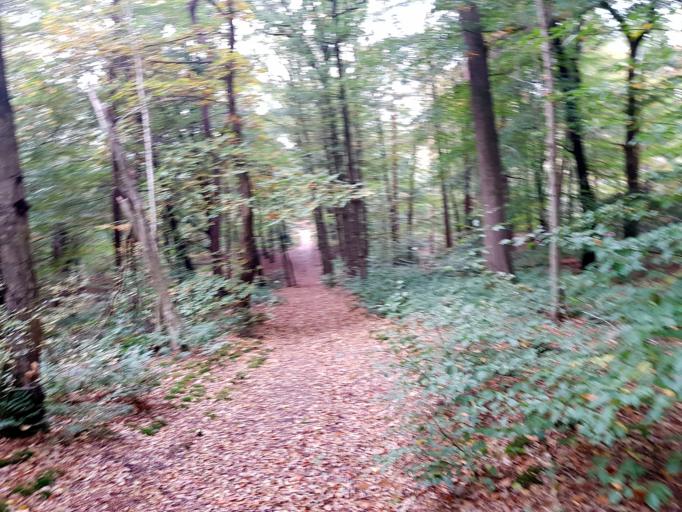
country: NL
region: Utrecht
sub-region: Gemeente Utrechtse Heuvelrug
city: Leersum
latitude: 52.0263
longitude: 5.3999
